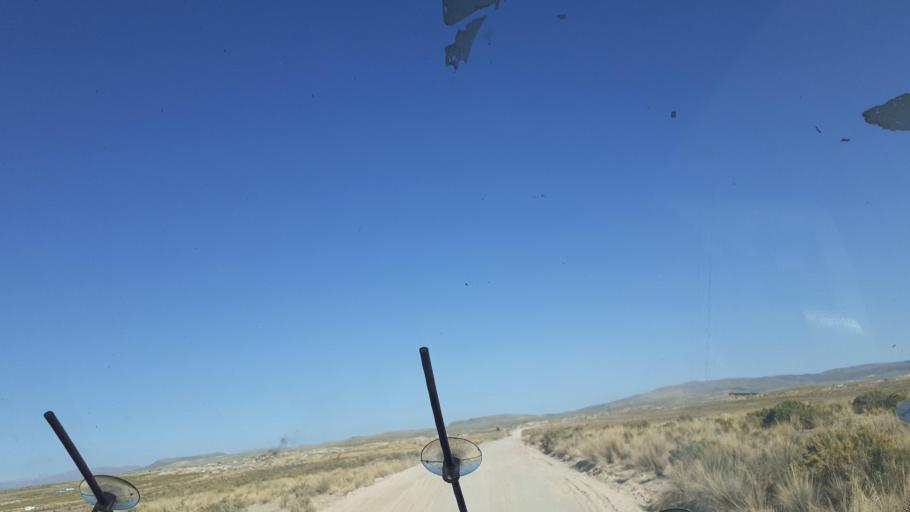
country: BO
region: La Paz
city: Tiahuanaco
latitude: -17.1159
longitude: -68.7933
